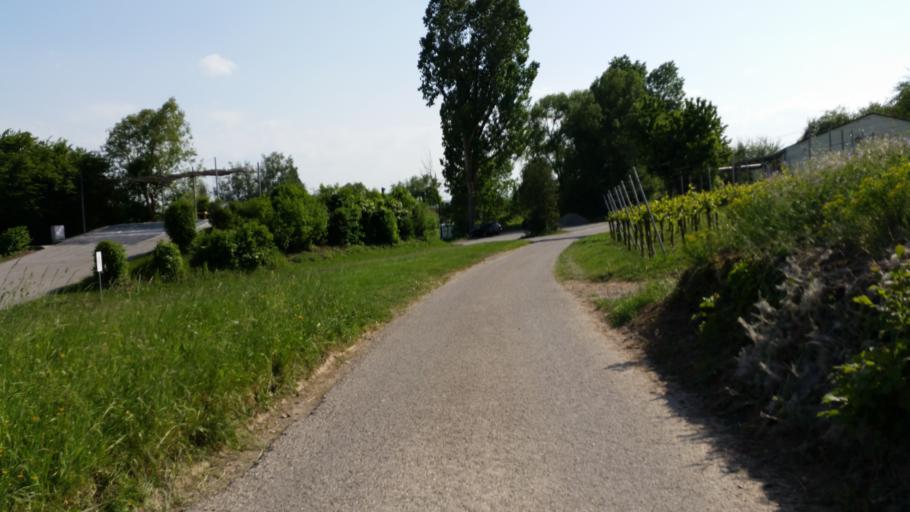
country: DE
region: Baden-Wuerttemberg
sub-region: Regierungsbezirk Stuttgart
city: Pleidelsheim
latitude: 48.9695
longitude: 9.1965
